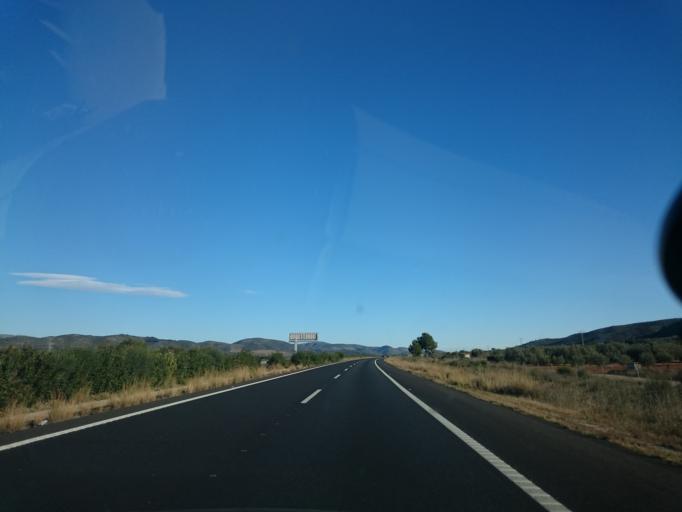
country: ES
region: Valencia
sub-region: Provincia de Castello
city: Alcala de Xivert
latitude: 40.3078
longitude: 0.2403
